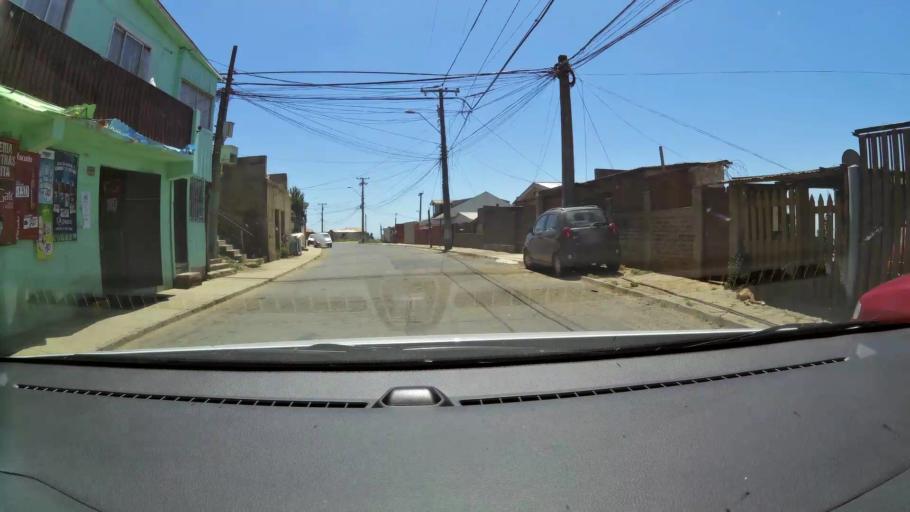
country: CL
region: Valparaiso
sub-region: Provincia de Valparaiso
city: Valparaiso
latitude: -33.0542
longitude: -71.6388
